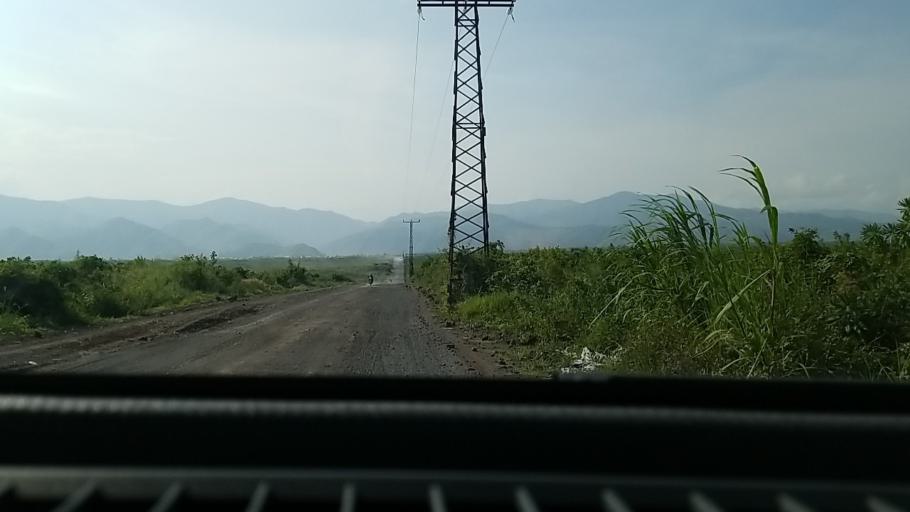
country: CD
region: Nord Kivu
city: Sake
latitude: -1.5865
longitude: 29.0895
